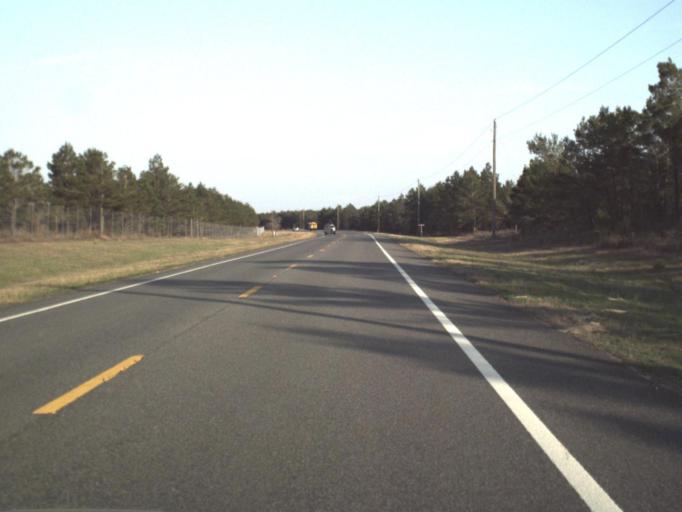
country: US
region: Florida
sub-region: Bay County
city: Lynn Haven
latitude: 30.4246
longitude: -85.6593
